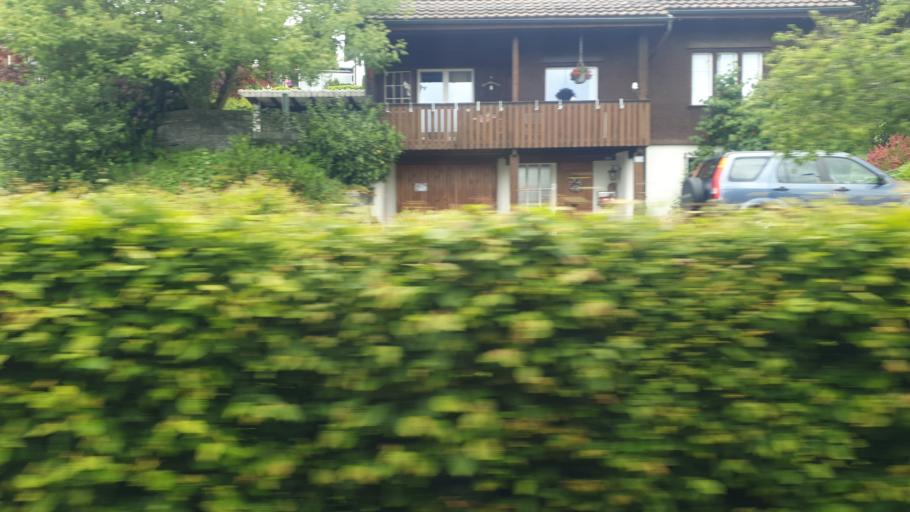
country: CH
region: Appenzell Ausserrhoden
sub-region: Bezirk Mittelland
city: Teufen
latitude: 47.3899
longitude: 9.3734
